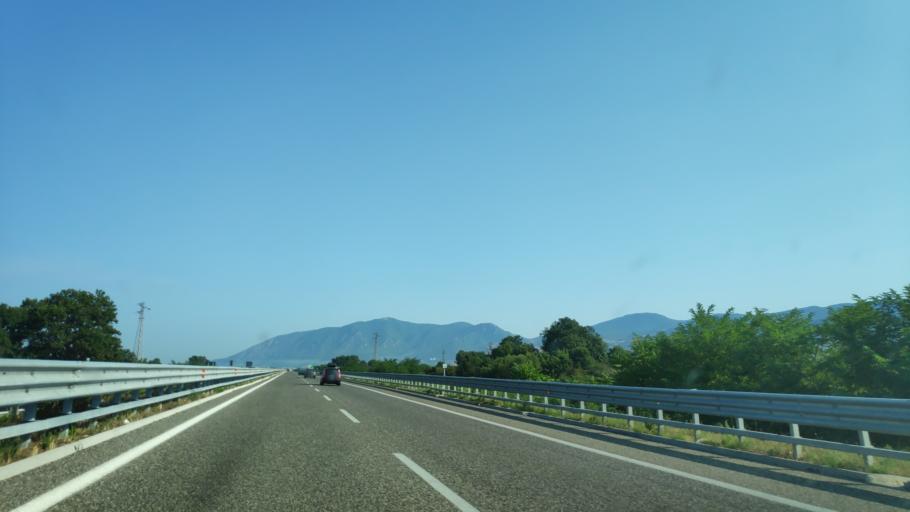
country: IT
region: Campania
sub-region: Provincia di Salerno
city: Padula
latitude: 40.3163
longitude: 15.6404
